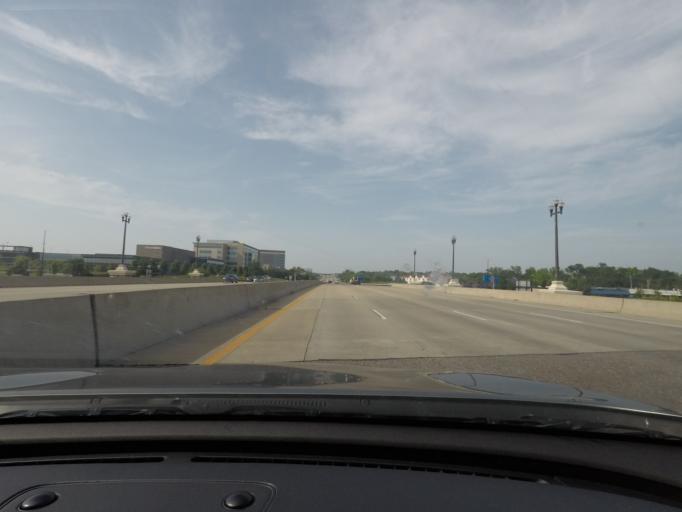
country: US
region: Missouri
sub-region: Saint Louis County
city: Maryland Heights
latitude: 38.7151
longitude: -90.4474
